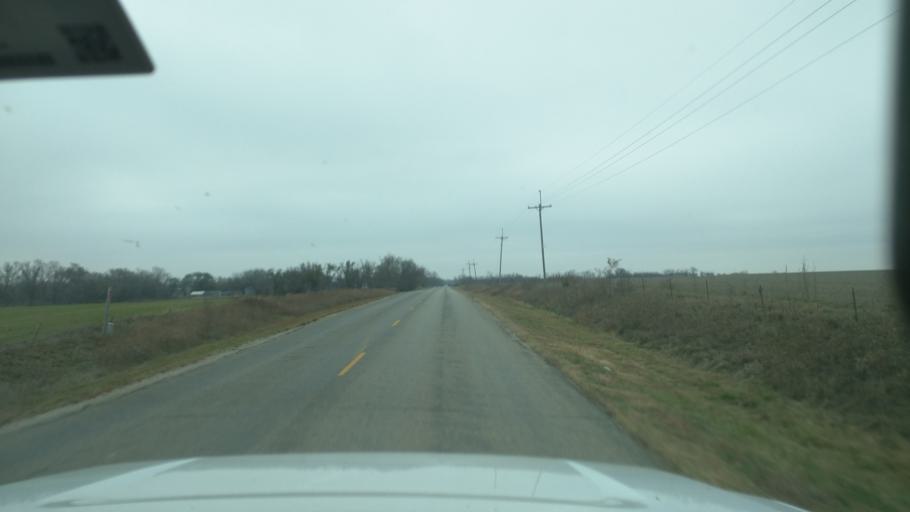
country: US
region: Kansas
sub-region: Lyon County
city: Emporia
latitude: 38.5352
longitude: -96.2614
